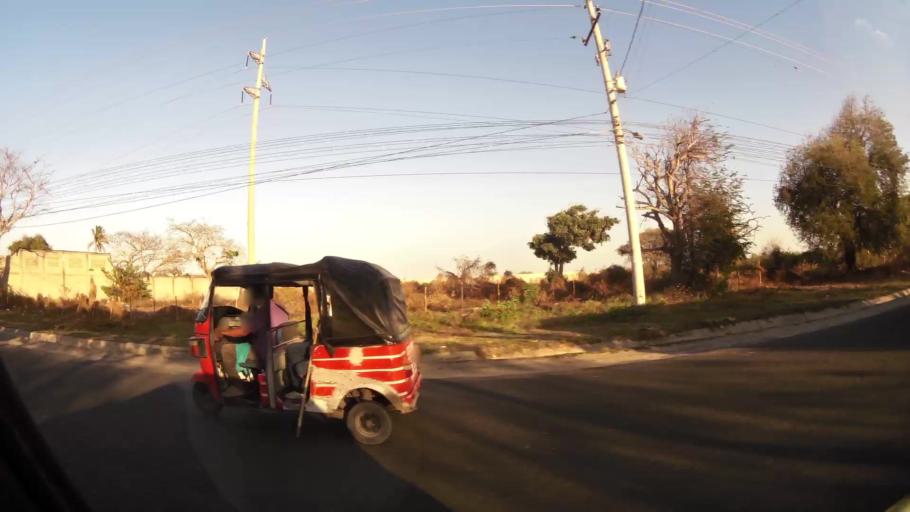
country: CO
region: Atlantico
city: Soledad
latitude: 10.8969
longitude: -74.8035
